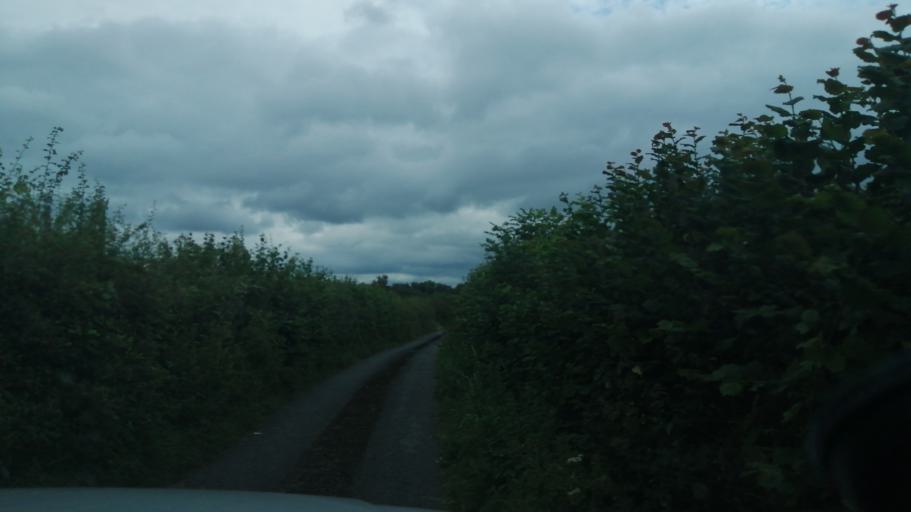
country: GB
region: England
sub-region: Herefordshire
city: Thruxton
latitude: 52.0138
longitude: -2.7904
